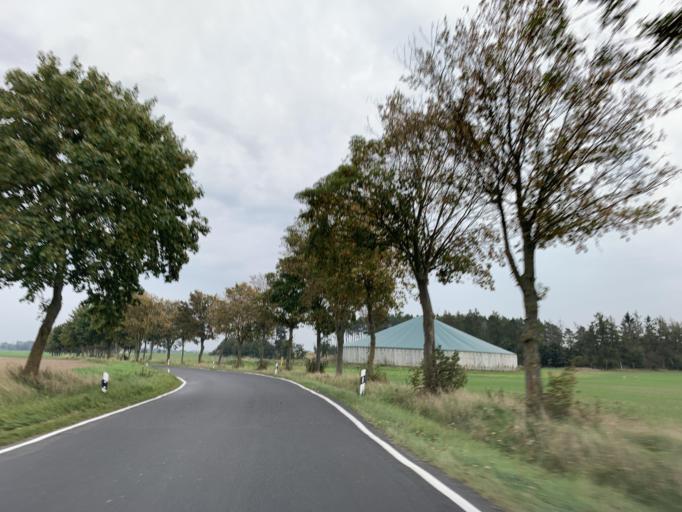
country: DE
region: Brandenburg
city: Mittenwalde
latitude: 53.3338
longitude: 13.6759
